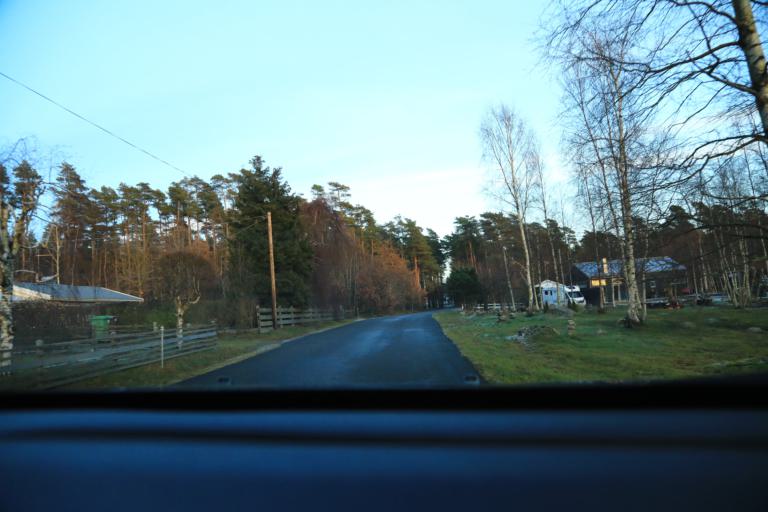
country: SE
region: Halland
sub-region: Varbergs Kommun
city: Varberg
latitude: 57.1941
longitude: 12.1882
